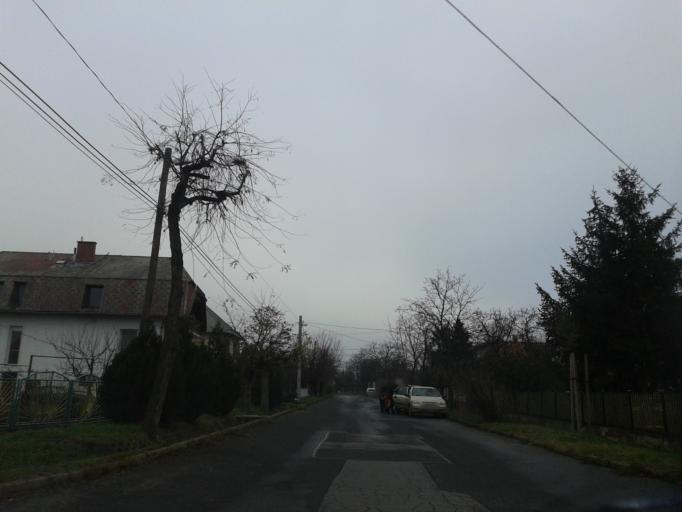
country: HU
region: Budapest
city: Budapest XXII. keruelet
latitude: 47.4232
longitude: 19.0155
